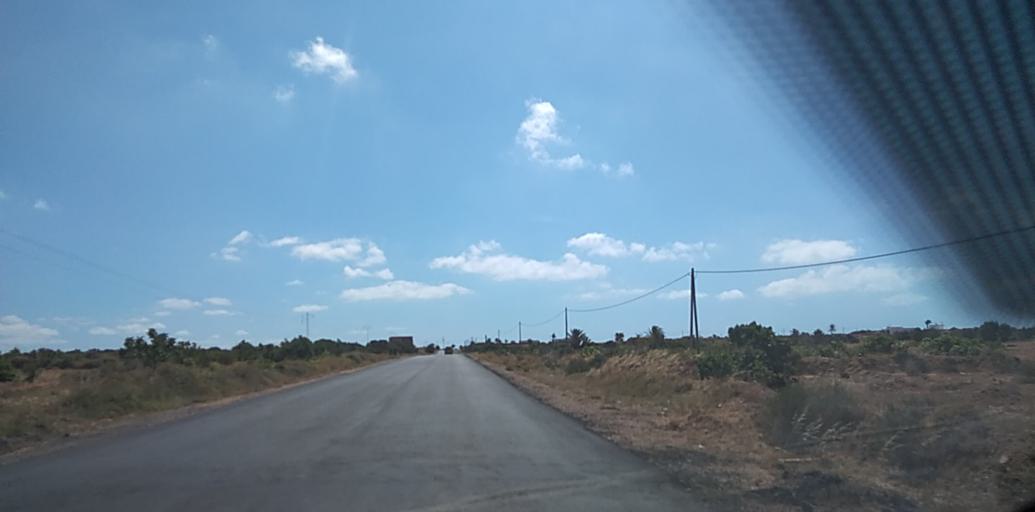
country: TN
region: Safaqis
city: Al Qarmadah
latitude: 34.6573
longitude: 11.0758
